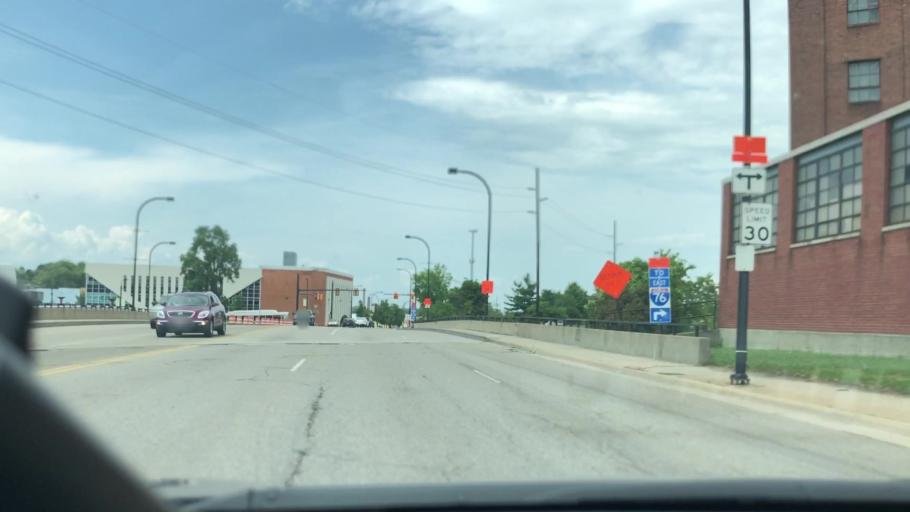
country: US
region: Ohio
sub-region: Summit County
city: Akron
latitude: 41.0551
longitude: -81.5281
